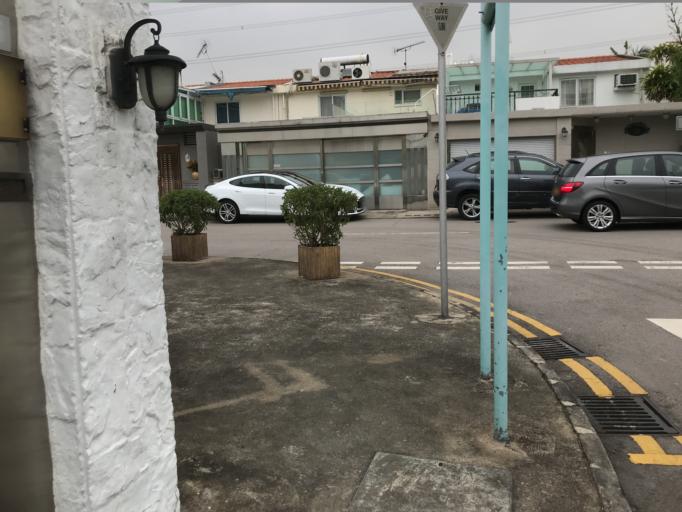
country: HK
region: Tai Po
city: Tai Po
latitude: 22.4654
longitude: 114.1527
